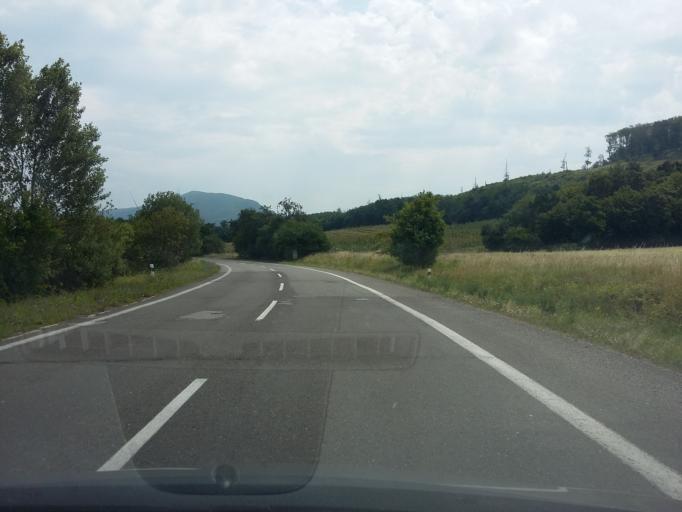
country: SK
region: Bratislavsky
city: Modra
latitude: 48.4589
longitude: 17.2037
